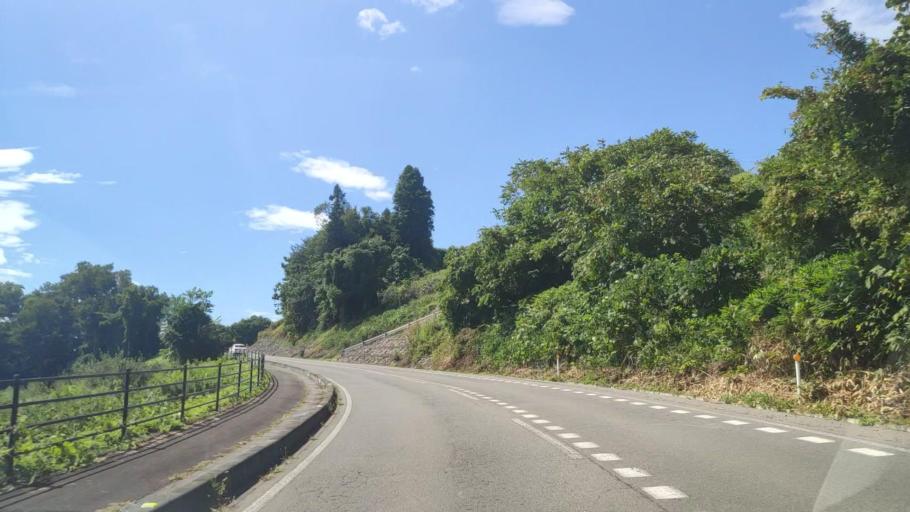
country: JP
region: Nagano
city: Suzaka
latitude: 36.7204
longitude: 138.2765
